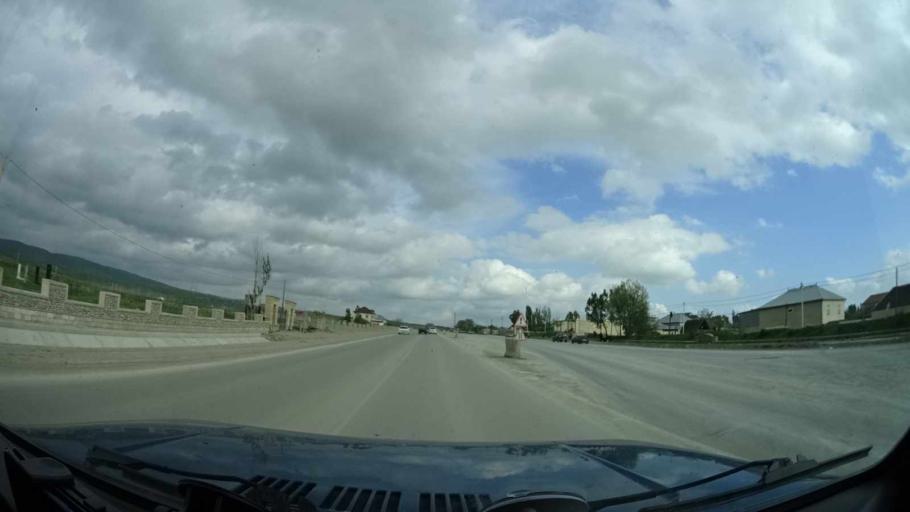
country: AZ
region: Samaxi
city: Shamakhi
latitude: 40.5913
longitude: 48.7055
